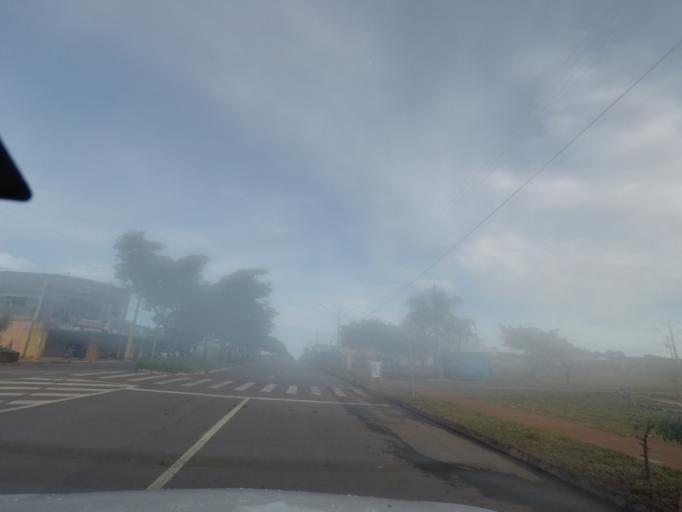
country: BR
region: Goias
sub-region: Aparecida De Goiania
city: Aparecida de Goiania
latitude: -16.7811
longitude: -49.3850
